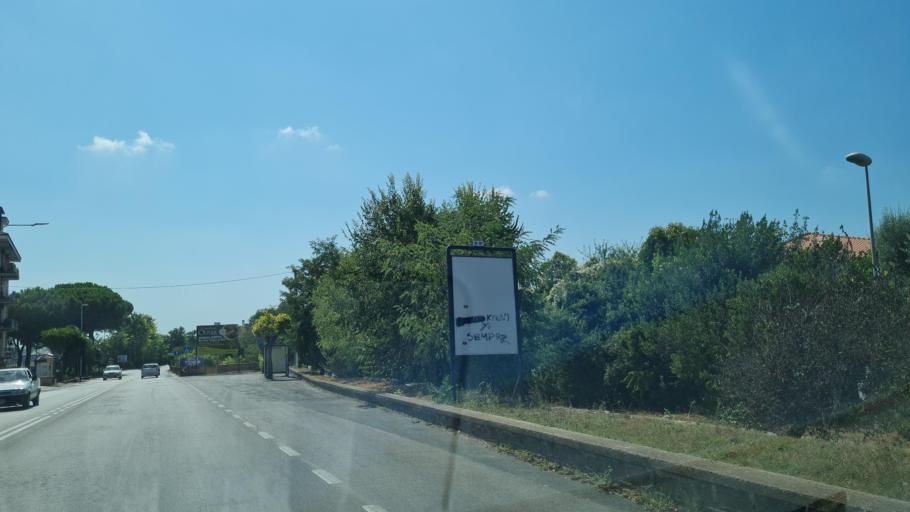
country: IT
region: Latium
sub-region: Provincia di Viterbo
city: Tarquinia
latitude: 42.2474
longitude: 11.7495
